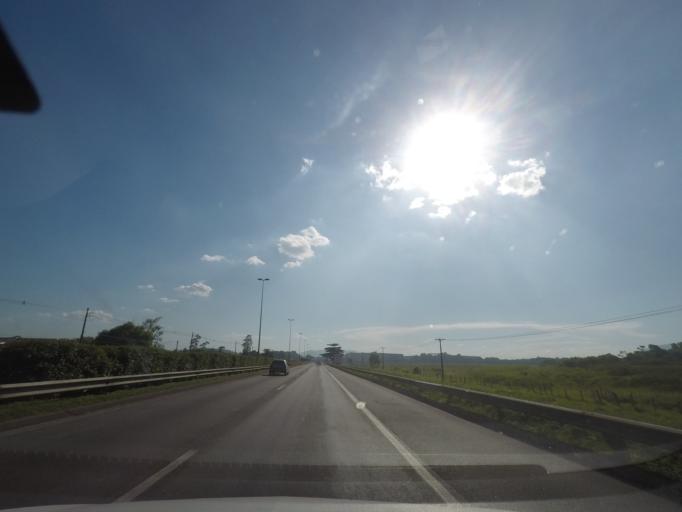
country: BR
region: Rio de Janeiro
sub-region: Duque De Caxias
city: Duque de Caxias
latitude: -22.6613
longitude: -43.2538
